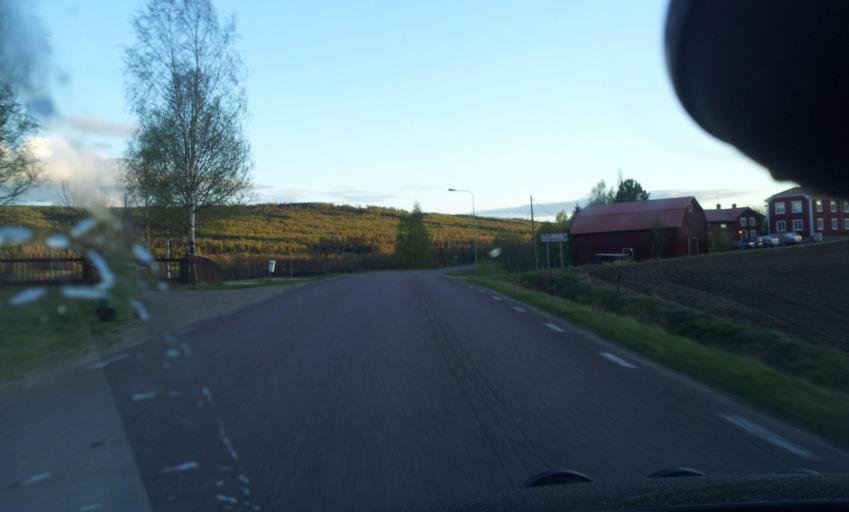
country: SE
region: Gaevleborg
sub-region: Bollnas Kommun
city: Bollnas
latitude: 61.4065
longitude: 16.5390
